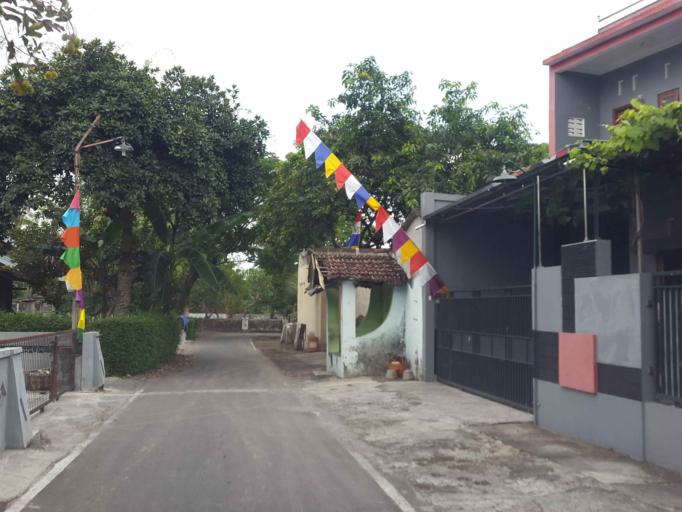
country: ID
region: Central Java
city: Jaten
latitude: -7.5900
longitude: 110.9364
